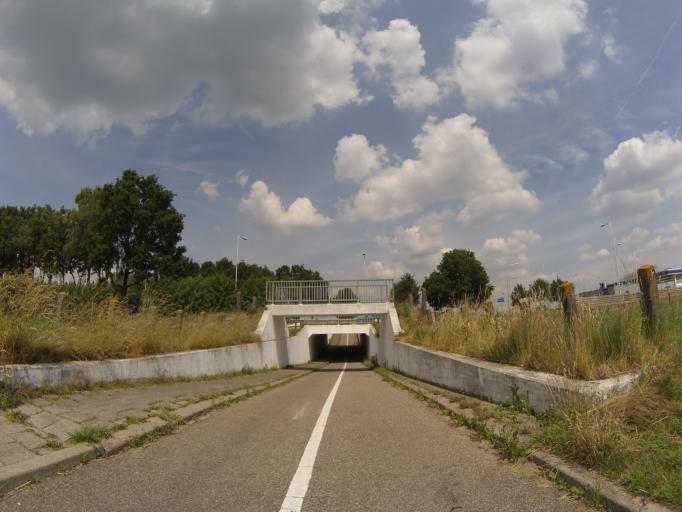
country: NL
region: Utrecht
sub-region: Gemeente De Bilt
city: De Bilt
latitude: 52.1404
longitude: 5.1632
